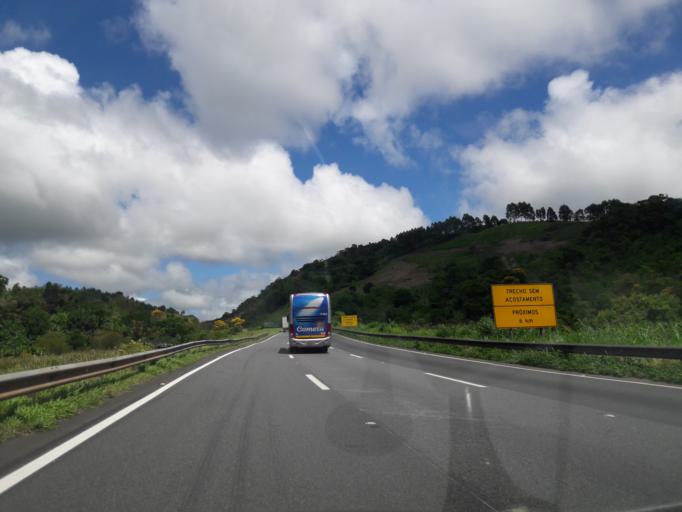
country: BR
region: Sao Paulo
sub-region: Cajati
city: Cajati
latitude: -24.9651
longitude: -48.4823
